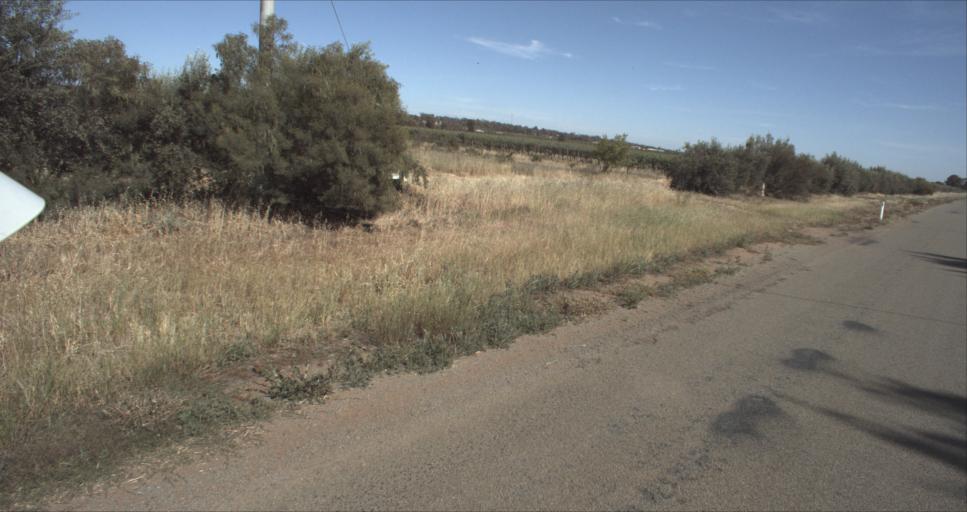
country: AU
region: New South Wales
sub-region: Leeton
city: Leeton
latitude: -34.5717
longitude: 146.4747
